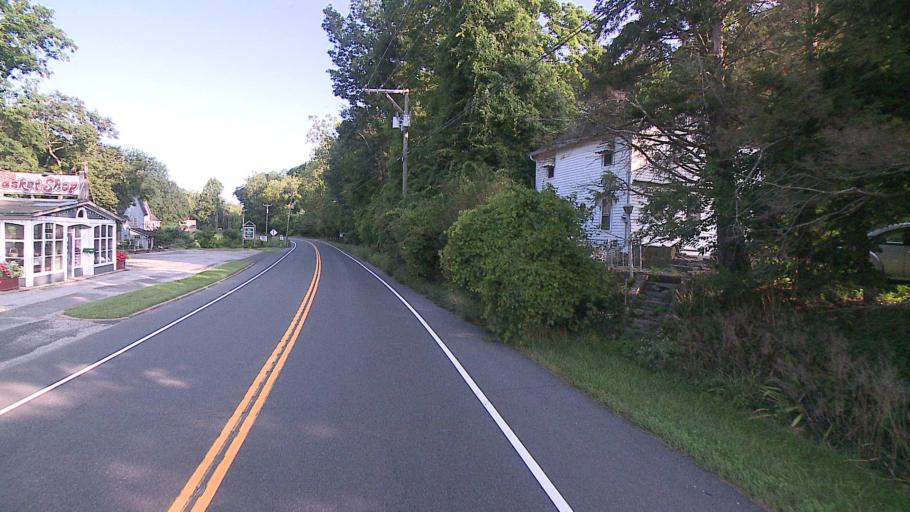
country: US
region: Connecticut
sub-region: Fairfield County
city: Sherman
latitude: 41.6488
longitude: -73.4843
